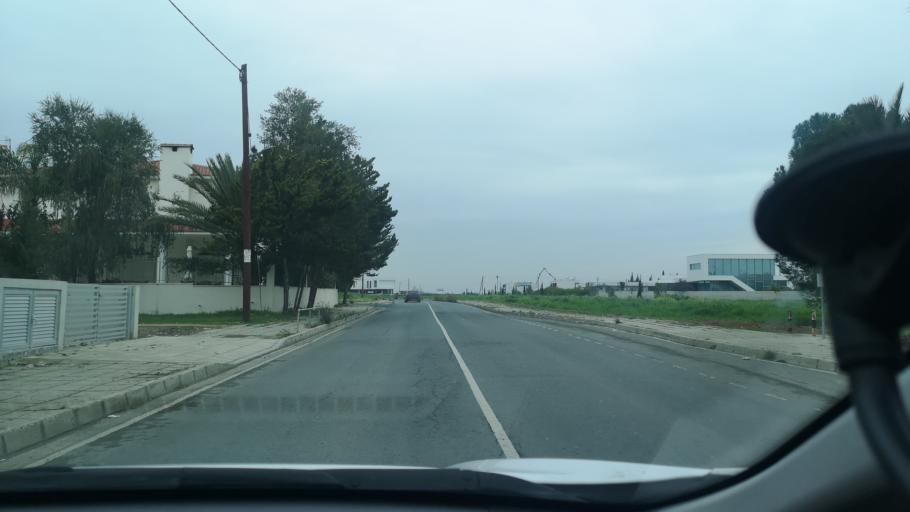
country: CY
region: Lefkosia
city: Tseri
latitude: 35.1080
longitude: 33.3533
